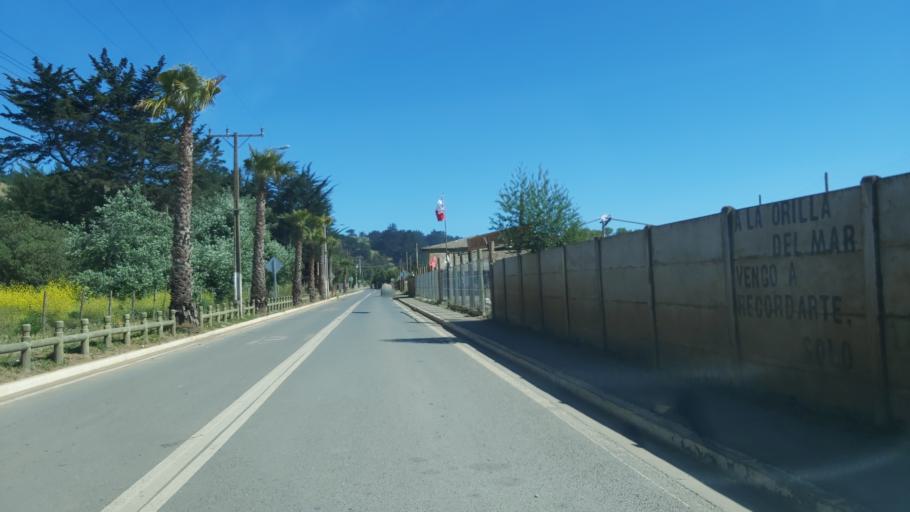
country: CL
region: Maule
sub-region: Provincia de Talca
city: Constitucion
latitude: -34.7631
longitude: -72.0800
